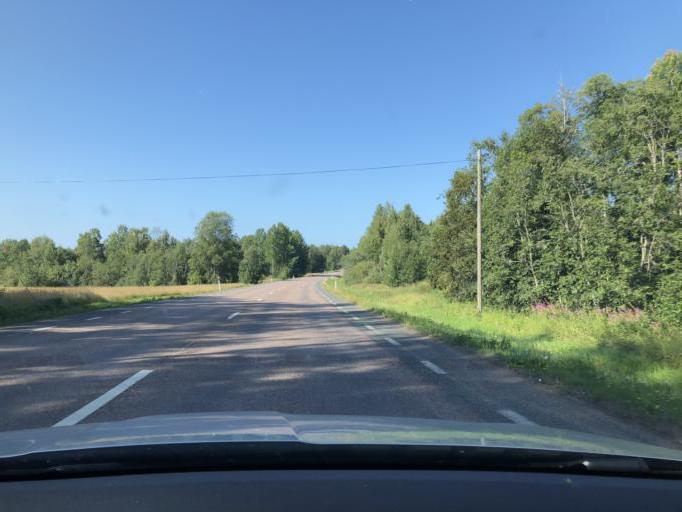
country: SE
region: Dalarna
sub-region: Faluns Kommun
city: Falun
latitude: 60.5072
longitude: 15.7384
